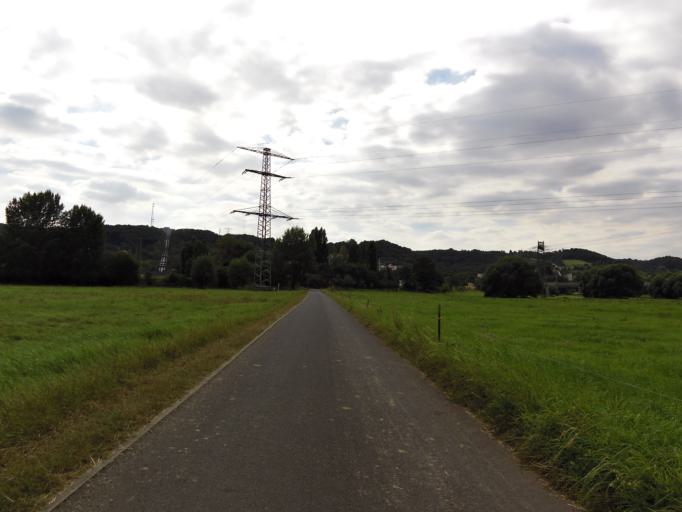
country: DE
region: Saxony
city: Coswig
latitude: 51.0965
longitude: 13.6133
